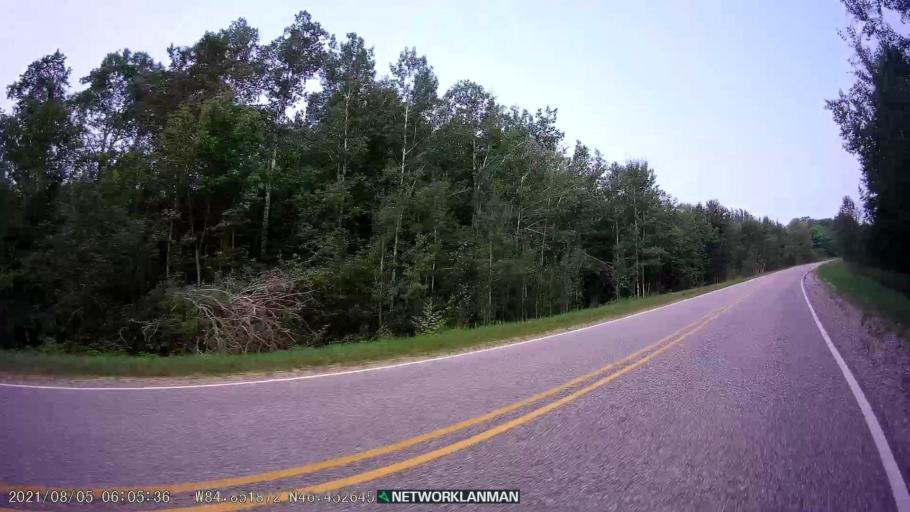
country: US
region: Michigan
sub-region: Chippewa County
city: Sault Ste. Marie
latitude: 46.4527
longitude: -84.8519
